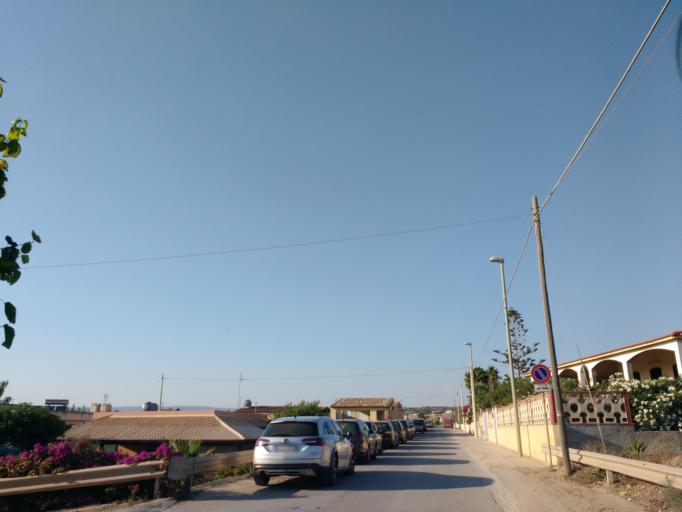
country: IT
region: Sicily
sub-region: Ragusa
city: Cava d'Aliga
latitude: 36.7352
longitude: 14.6806
